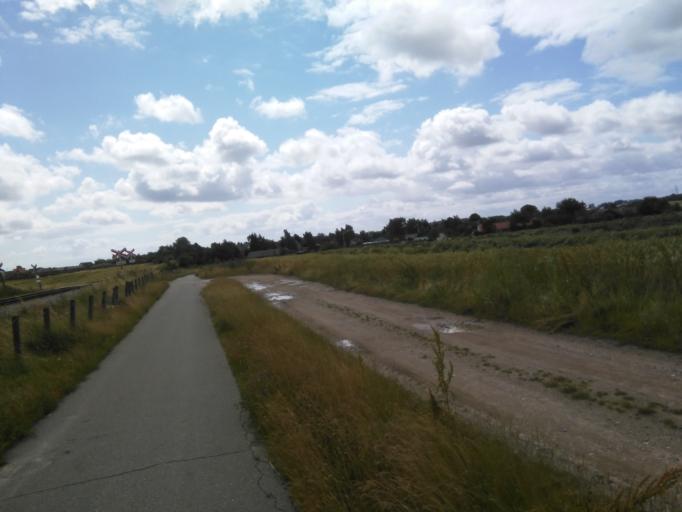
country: DK
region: Central Jutland
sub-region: Arhus Kommune
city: Marslet
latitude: 56.0789
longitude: 10.1524
